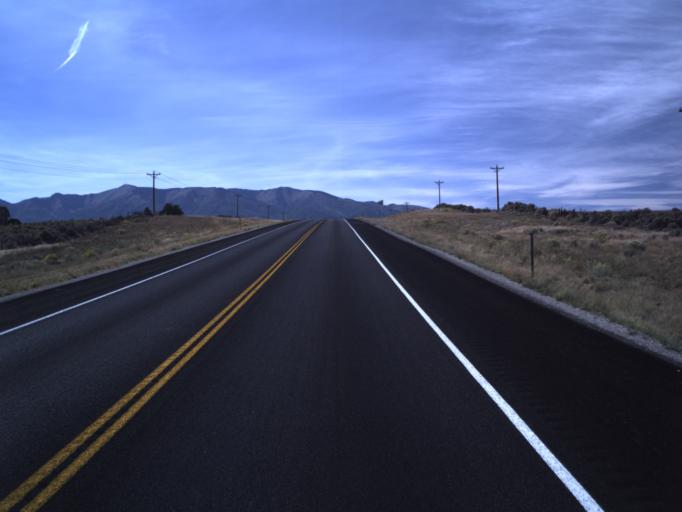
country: US
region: Utah
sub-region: San Juan County
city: Monticello
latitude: 37.8729
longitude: -109.2820
